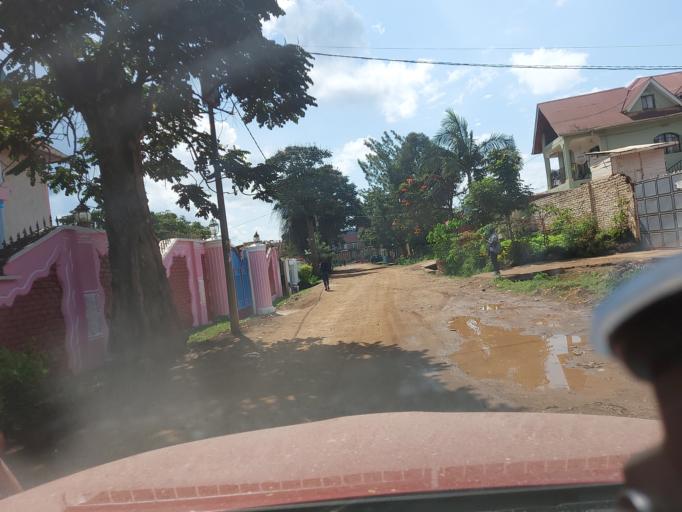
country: RW
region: Western Province
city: Cyangugu
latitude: -2.4983
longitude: 28.8855
